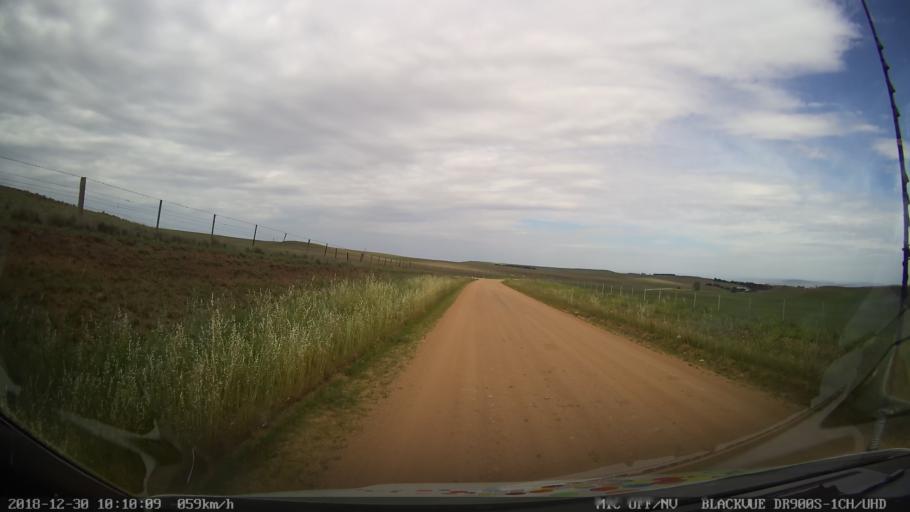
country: AU
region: New South Wales
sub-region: Cooma-Monaro
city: Cooma
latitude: -36.5504
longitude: 149.0977
